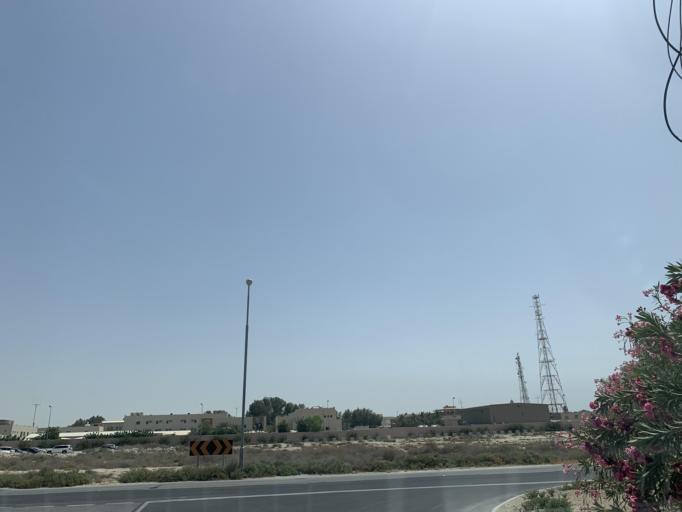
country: BH
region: Northern
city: Ar Rifa'
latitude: 26.1471
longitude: 50.5472
